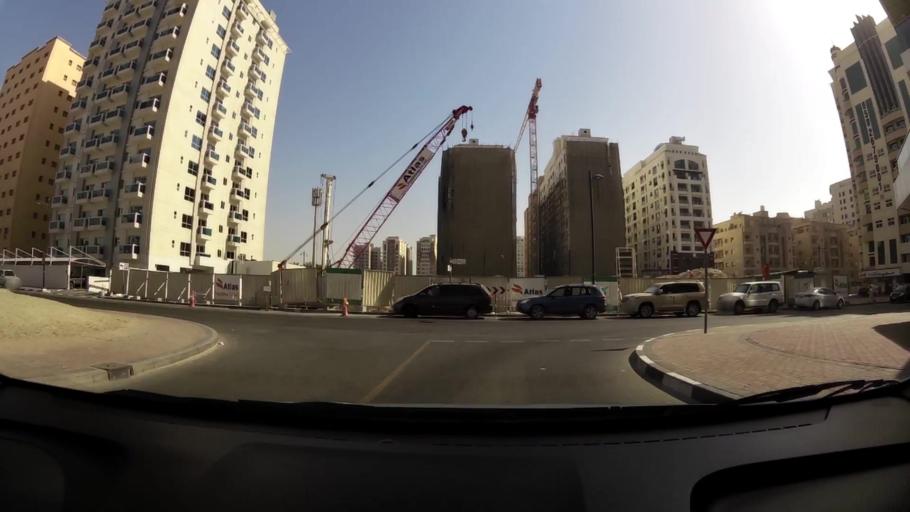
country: AE
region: Ash Shariqah
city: Sharjah
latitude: 25.2928
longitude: 55.3818
